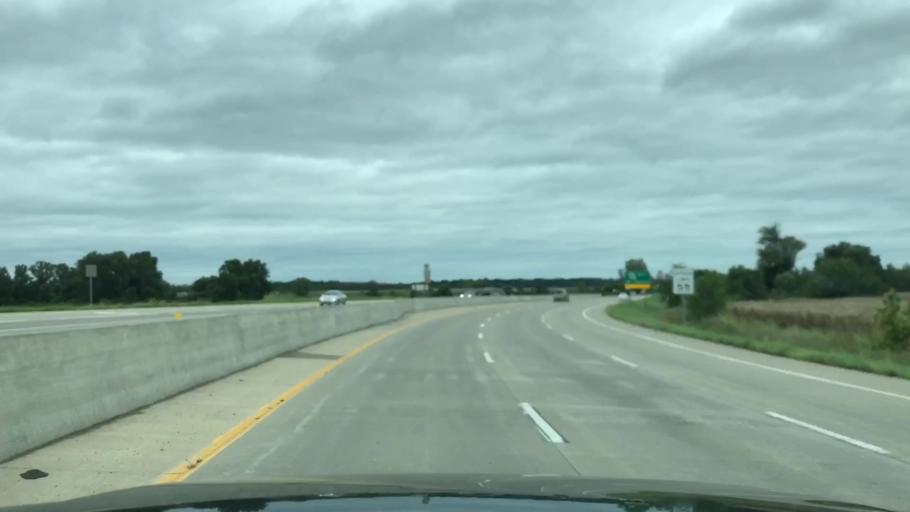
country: US
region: Missouri
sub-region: Saint Louis County
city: Maryland Heights
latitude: 38.7151
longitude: -90.4995
